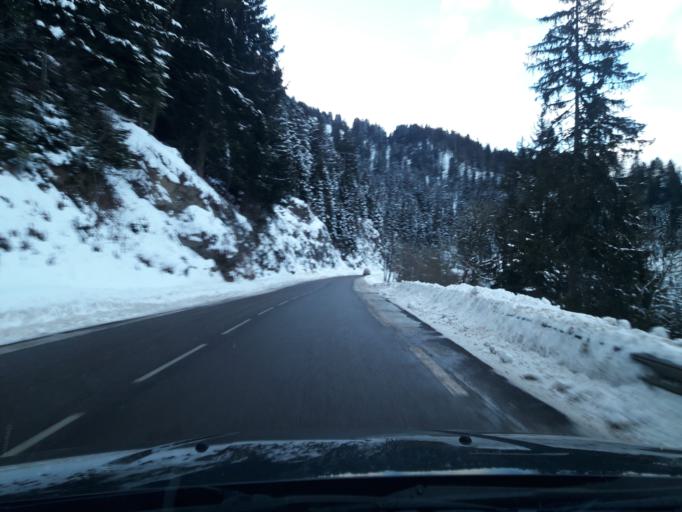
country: FR
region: Rhone-Alpes
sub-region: Departement de l'Isere
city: Revel
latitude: 45.1370
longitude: 5.8808
